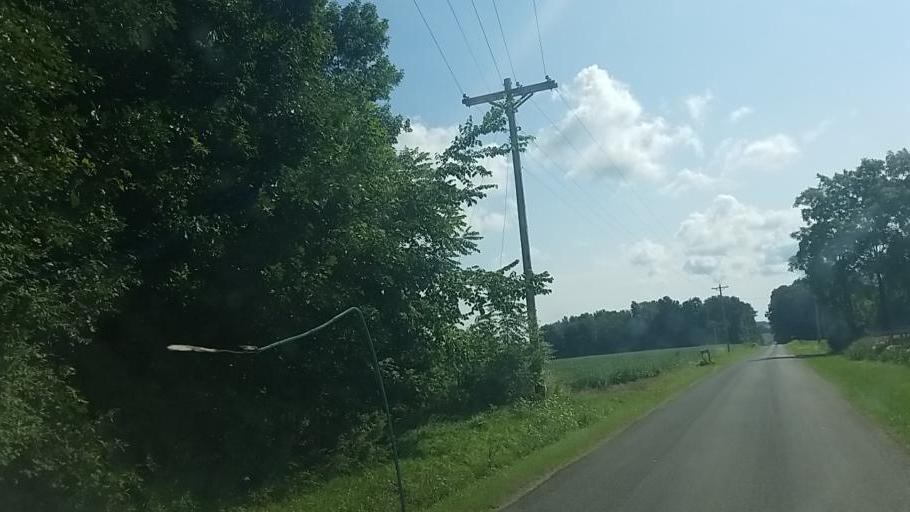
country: US
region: Ohio
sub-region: Ashland County
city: Ashland
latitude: 40.7988
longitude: -82.3283
